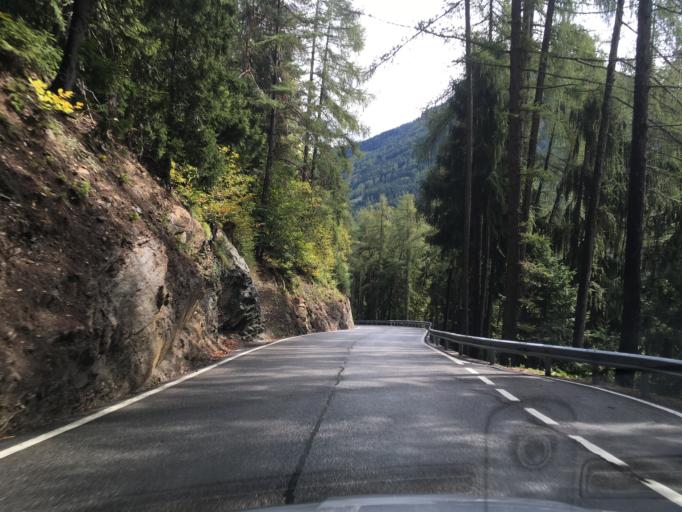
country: IT
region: Trentino-Alto Adige
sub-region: Bolzano
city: San Leonardo in Passiria
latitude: 46.8194
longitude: 11.2517
